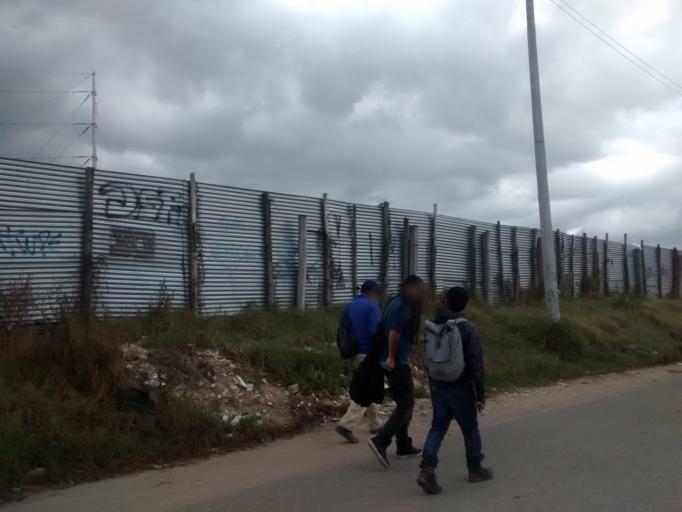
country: CO
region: Cundinamarca
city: Cota
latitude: 4.7302
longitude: -74.1031
